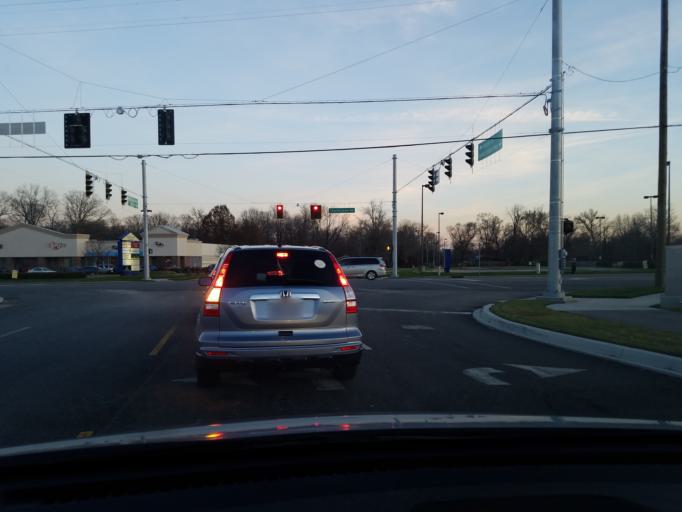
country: US
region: Indiana
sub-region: Clark County
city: Sellersburg
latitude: 38.3540
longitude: -85.7928
